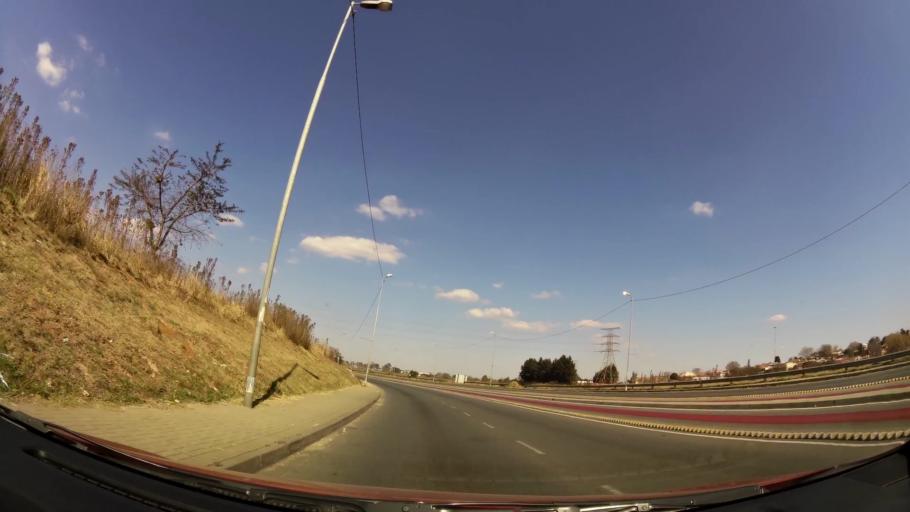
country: ZA
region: Gauteng
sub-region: City of Johannesburg Metropolitan Municipality
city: Soweto
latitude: -26.2422
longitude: 27.9112
